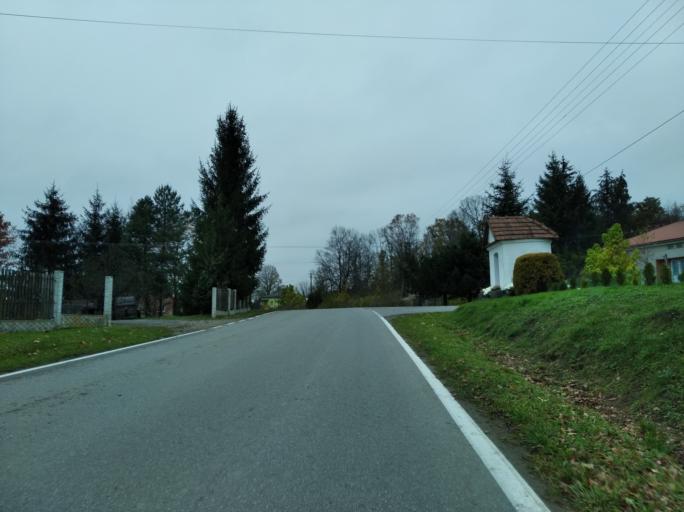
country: PL
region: Subcarpathian Voivodeship
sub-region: Powiat krosnienski
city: Leki
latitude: 49.8079
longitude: 21.6602
